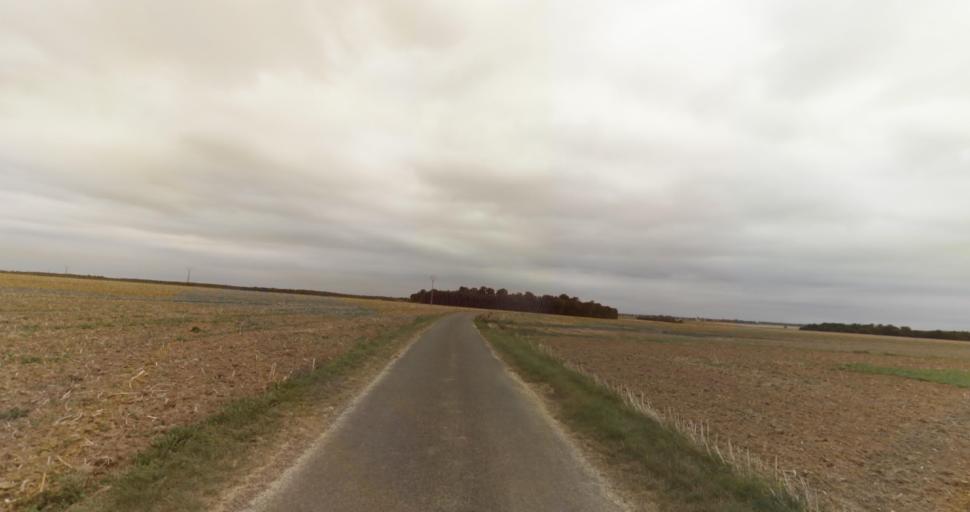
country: FR
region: Haute-Normandie
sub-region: Departement de l'Eure
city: La Couture-Boussey
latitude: 48.9285
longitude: 1.3628
